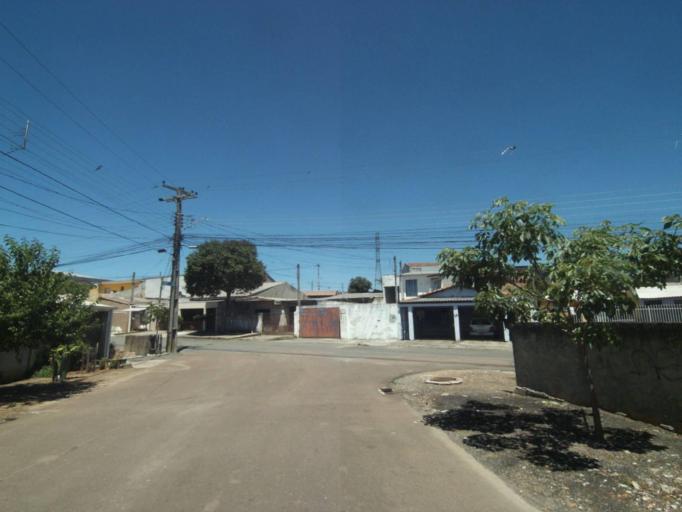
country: BR
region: Parana
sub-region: Curitiba
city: Curitiba
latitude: -25.4763
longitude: -49.3497
